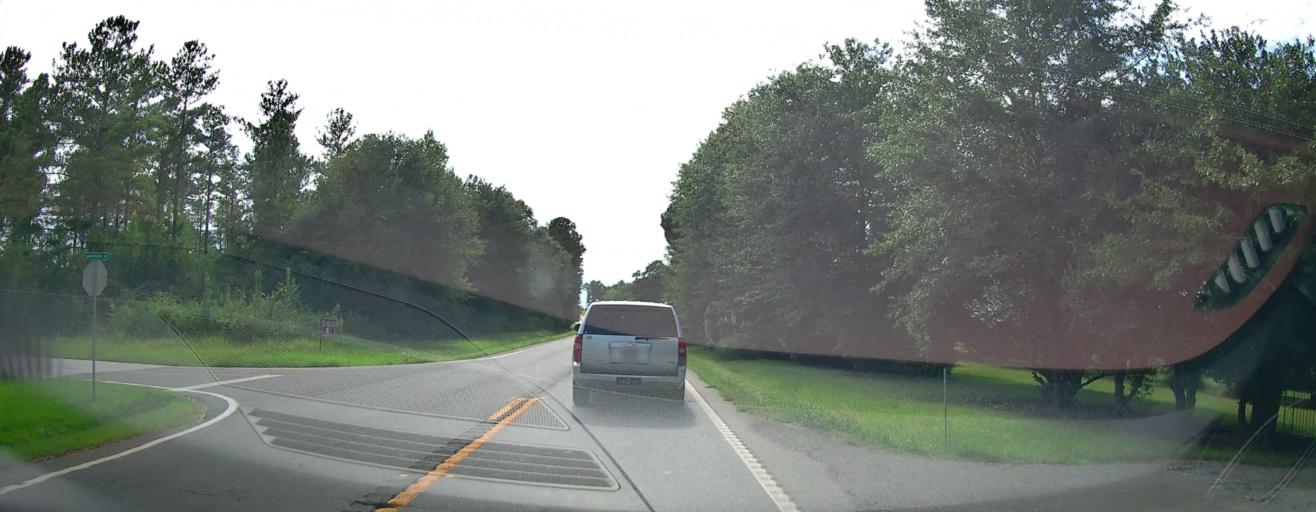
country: US
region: Georgia
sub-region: Meriwether County
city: Manchester
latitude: 32.9930
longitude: -84.5130
